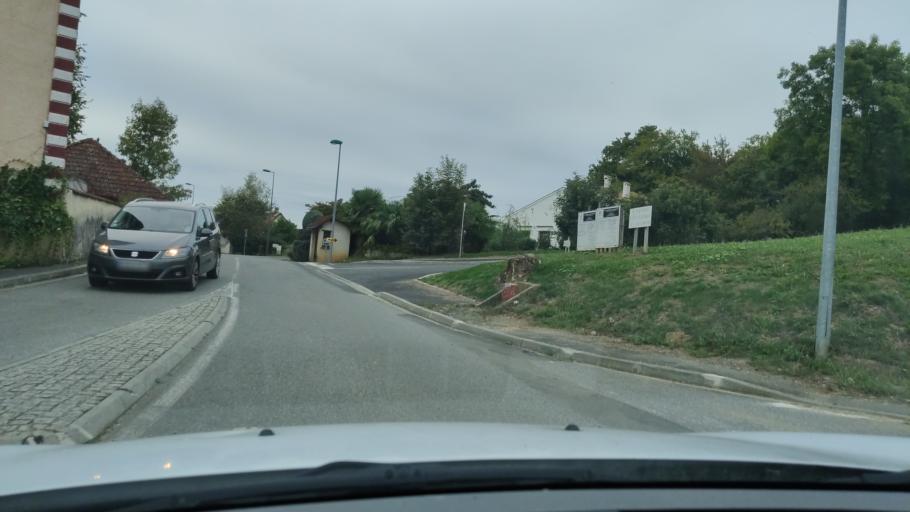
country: FR
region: Aquitaine
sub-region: Departement des Pyrenees-Atlantiques
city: Sauvagnon
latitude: 43.4049
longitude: -0.3794
